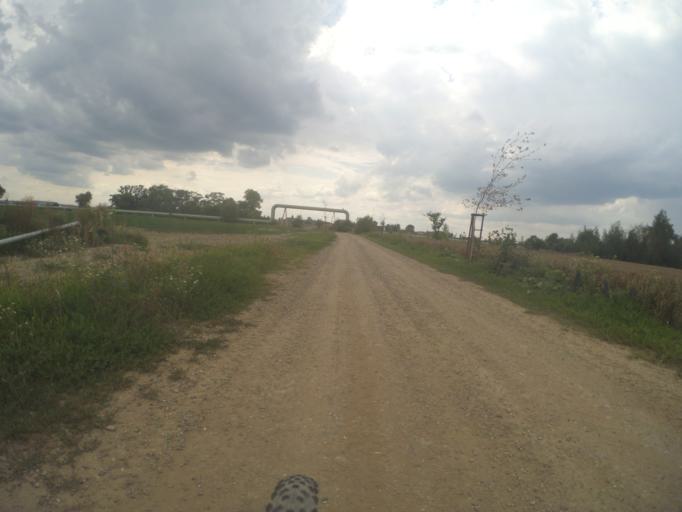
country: CZ
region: Central Bohemia
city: Luzec nad Vltavou
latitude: 50.3103
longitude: 14.4447
